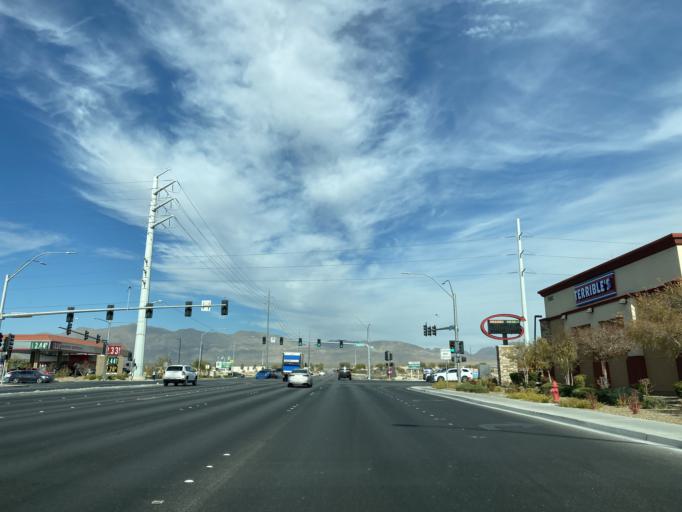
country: US
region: Nevada
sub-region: Clark County
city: Nellis Air Force Base
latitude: 36.2682
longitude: -115.1169
